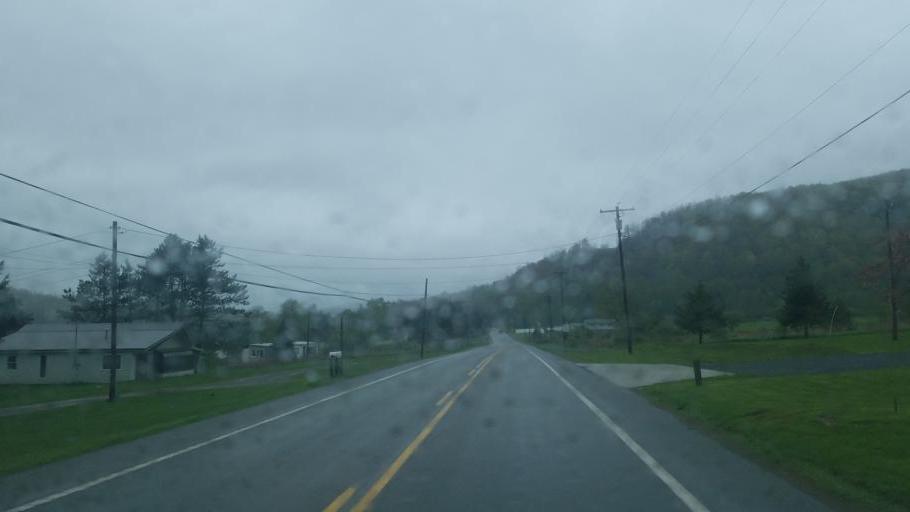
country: US
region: Pennsylvania
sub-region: Potter County
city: Coudersport
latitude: 41.7616
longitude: -78.1143
